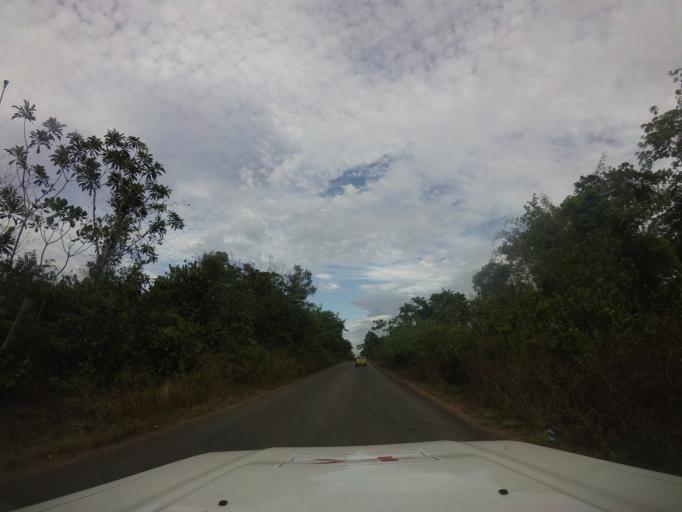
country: LR
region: Bomi
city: Tubmanburg
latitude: 6.6898
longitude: -10.8836
